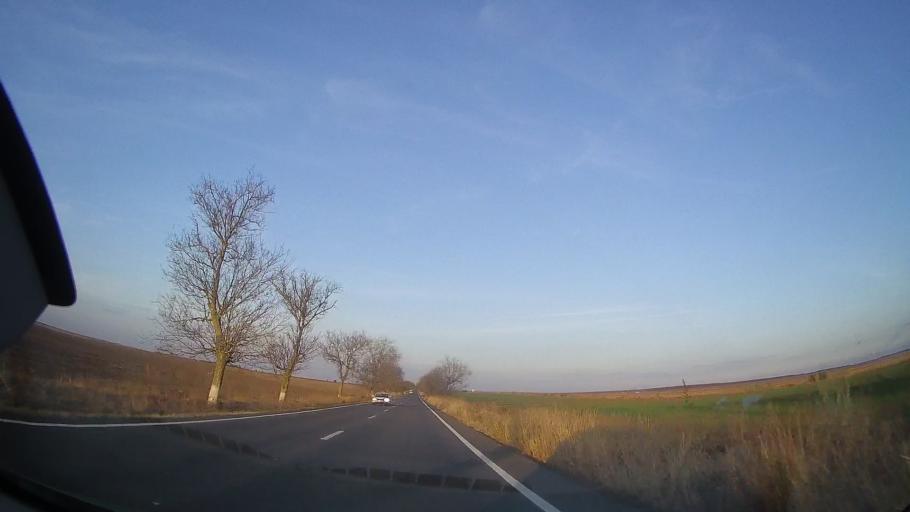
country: RO
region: Constanta
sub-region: Comuna Amzacea
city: Amzacea
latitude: 43.9442
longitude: 28.3749
